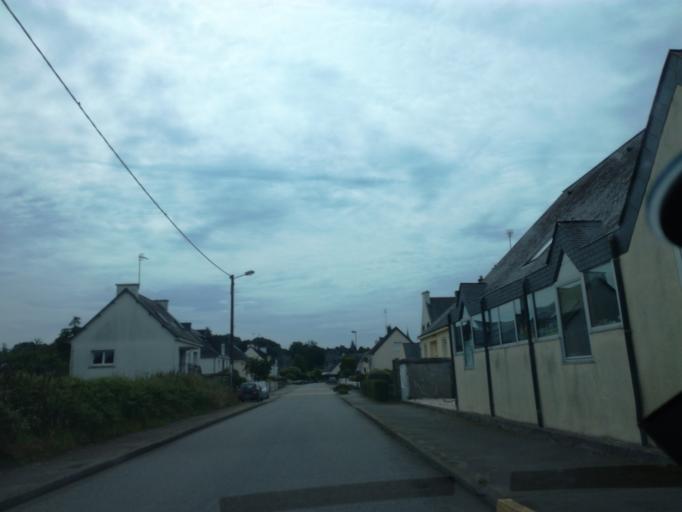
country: FR
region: Brittany
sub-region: Departement du Morbihan
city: Saint-Thuriau
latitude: 48.0199
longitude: -2.9525
